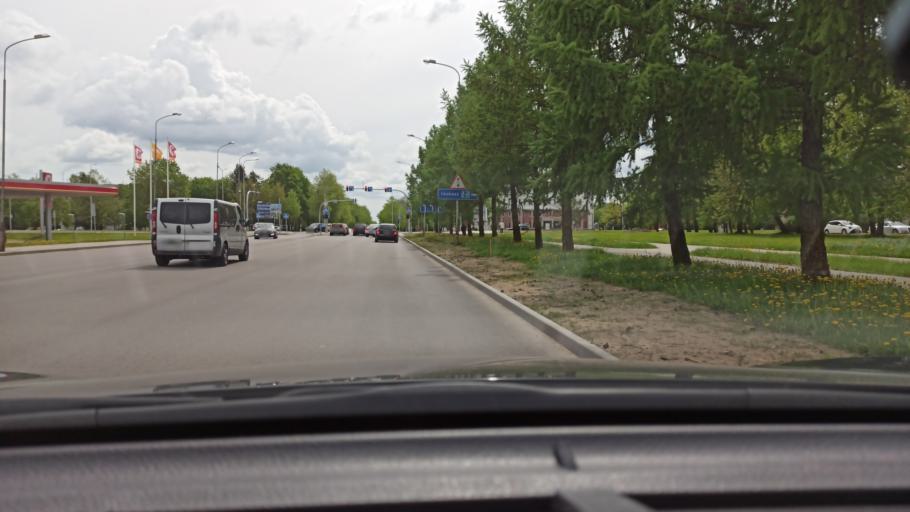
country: LT
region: Siauliu apskritis
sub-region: Siauliai
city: Siauliai
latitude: 55.9130
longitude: 23.2727
